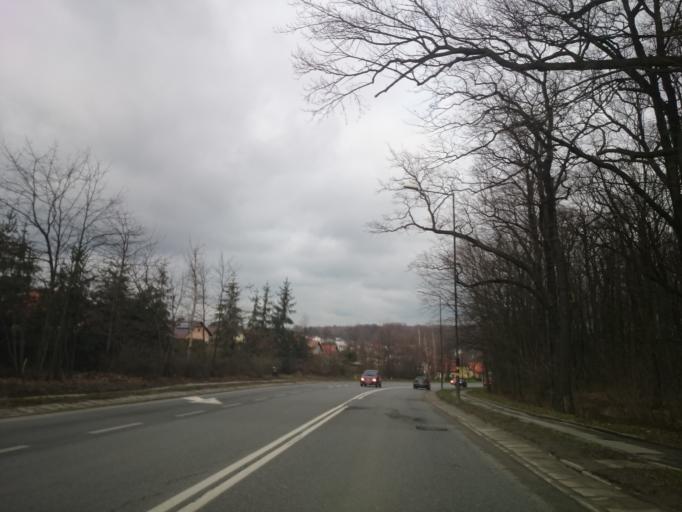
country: PL
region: Opole Voivodeship
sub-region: Powiat nyski
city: Nysa
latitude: 50.4803
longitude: 17.3055
